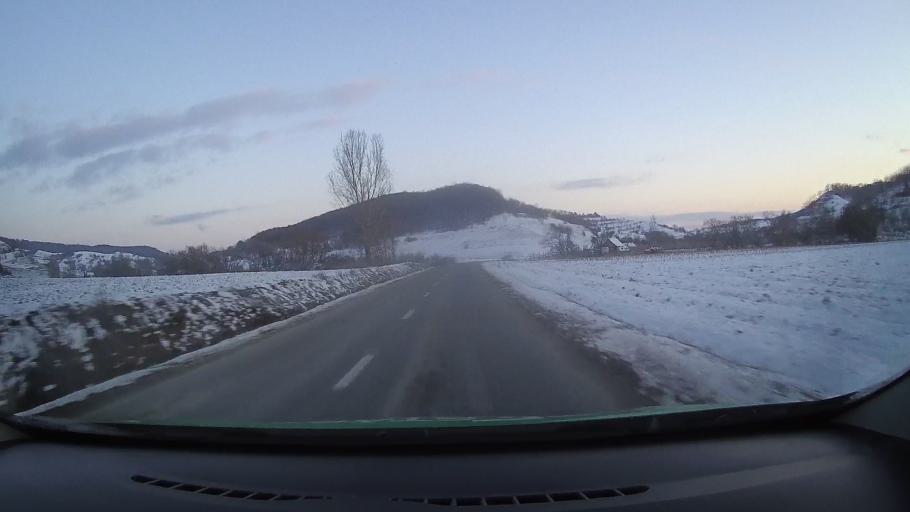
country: RO
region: Sibiu
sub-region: Comuna Alma
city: Alma
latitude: 46.2019
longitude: 24.4678
